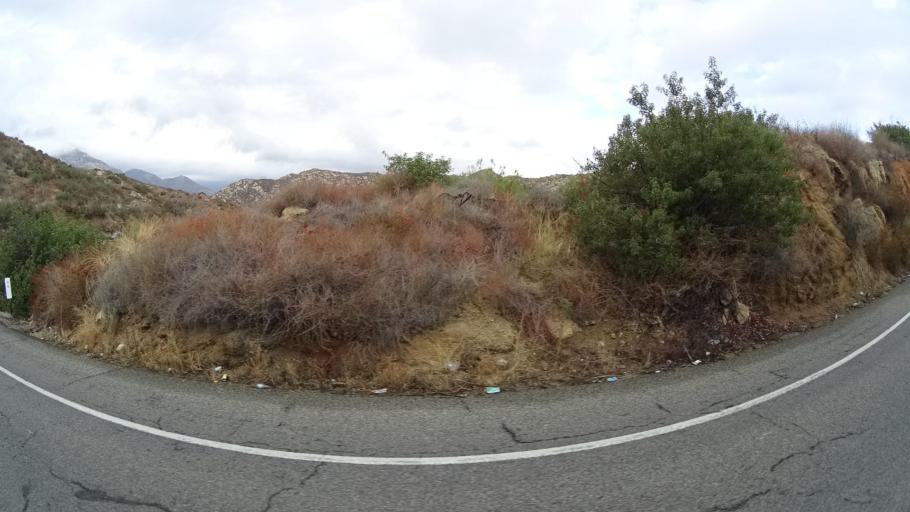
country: MX
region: Baja California
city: Tecate
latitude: 32.6017
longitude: -116.6333
